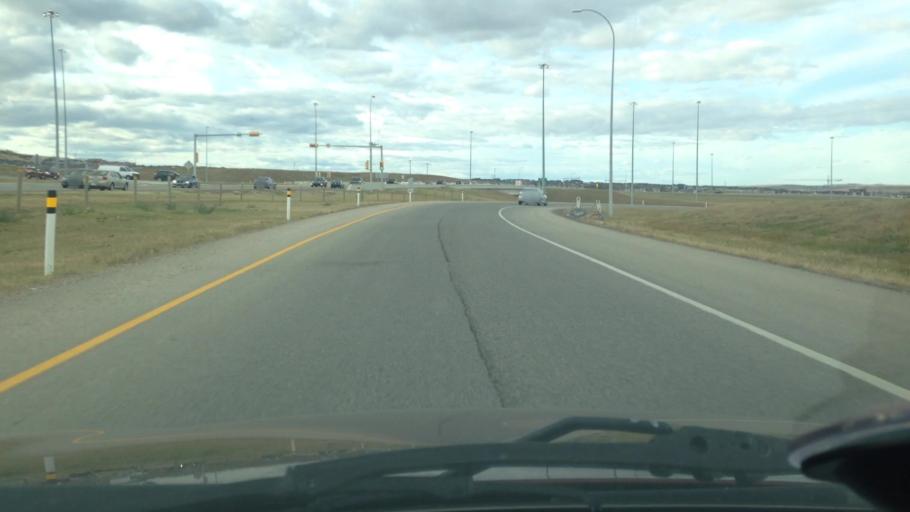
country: CA
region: Alberta
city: Calgary
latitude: 51.1499
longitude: -114.1386
